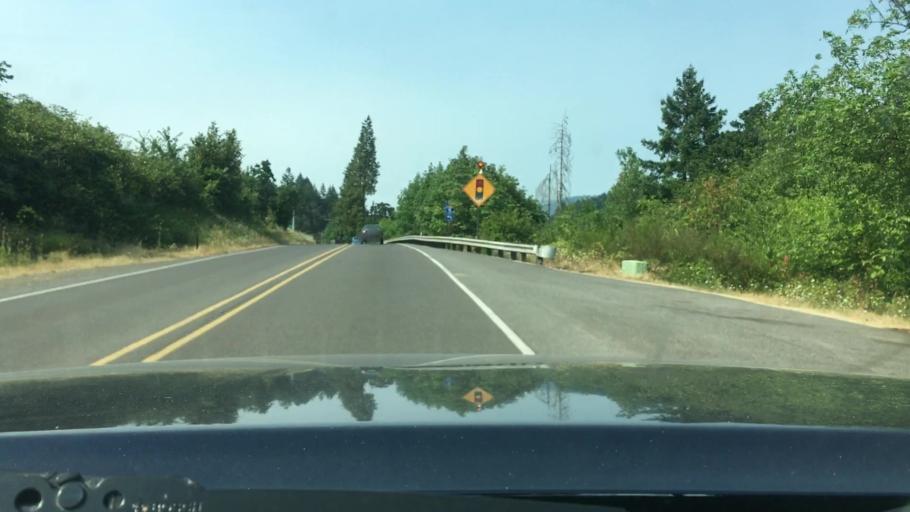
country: US
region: Oregon
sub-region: Lane County
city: Springfield
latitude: 44.0228
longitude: -123.0267
